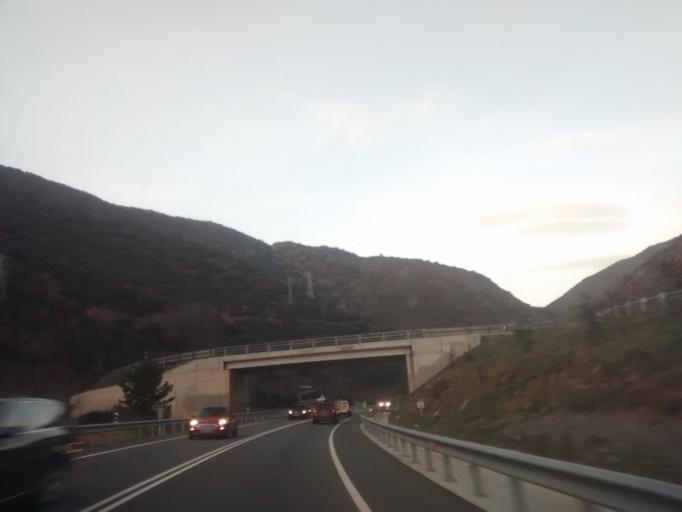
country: ES
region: Catalonia
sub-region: Provincia de Lleida
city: la Seu d'Urgell
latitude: 42.3941
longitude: 1.4612
